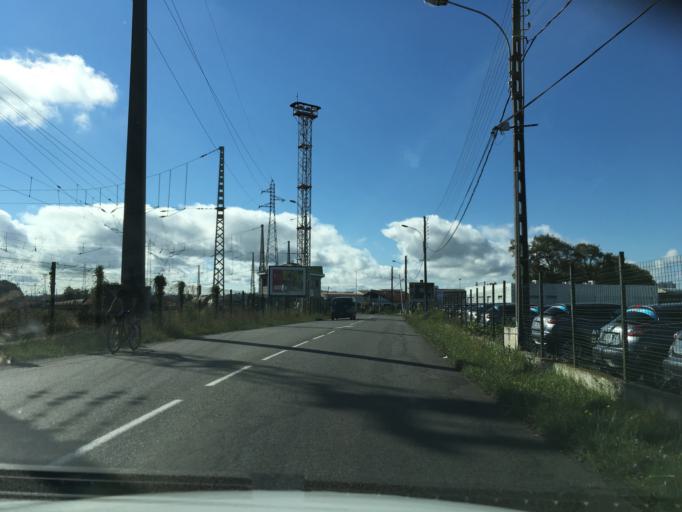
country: FR
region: Aquitaine
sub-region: Departement des Pyrenees-Atlantiques
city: Bayonne
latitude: 43.5043
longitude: -1.4850
